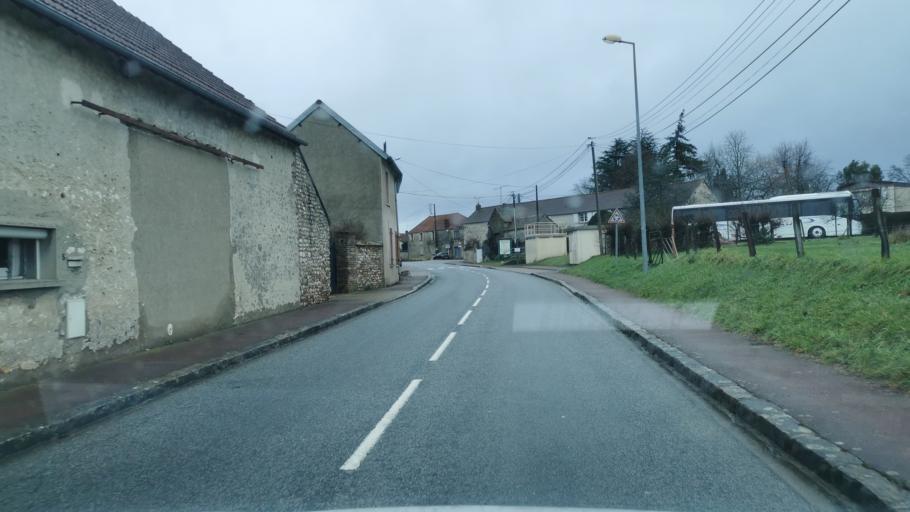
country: FR
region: Ile-de-France
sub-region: Departement des Yvelines
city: Longnes
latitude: 48.9184
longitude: 1.5877
